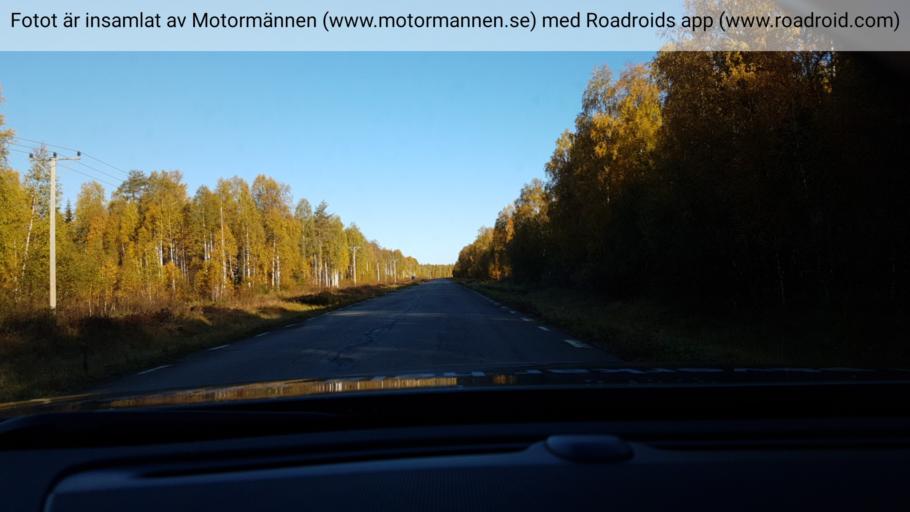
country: SE
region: Norrbotten
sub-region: Bodens Kommun
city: Boden
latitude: 65.9139
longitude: 21.6606
